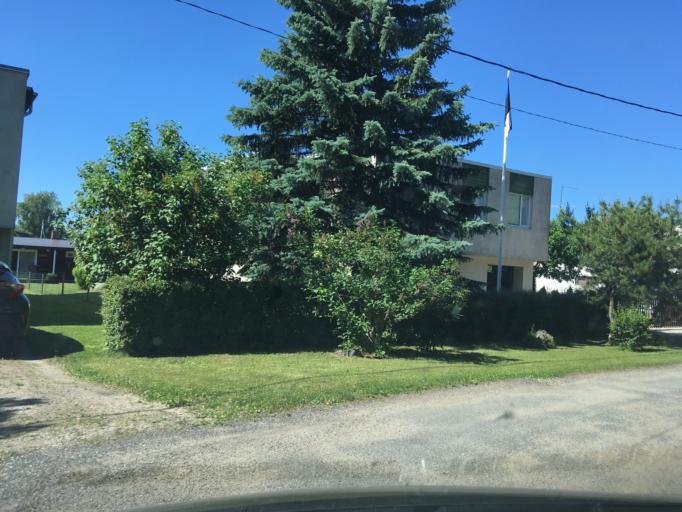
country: EE
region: Harju
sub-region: Raasiku vald
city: Raasiku
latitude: 59.1808
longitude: 25.1714
